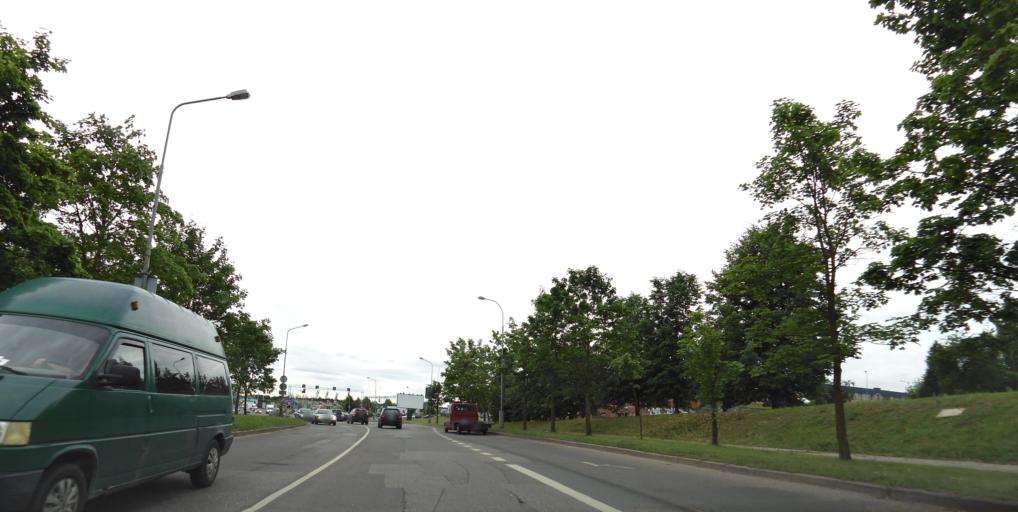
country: LT
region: Vilnius County
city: Seskine
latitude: 54.7123
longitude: 25.2563
